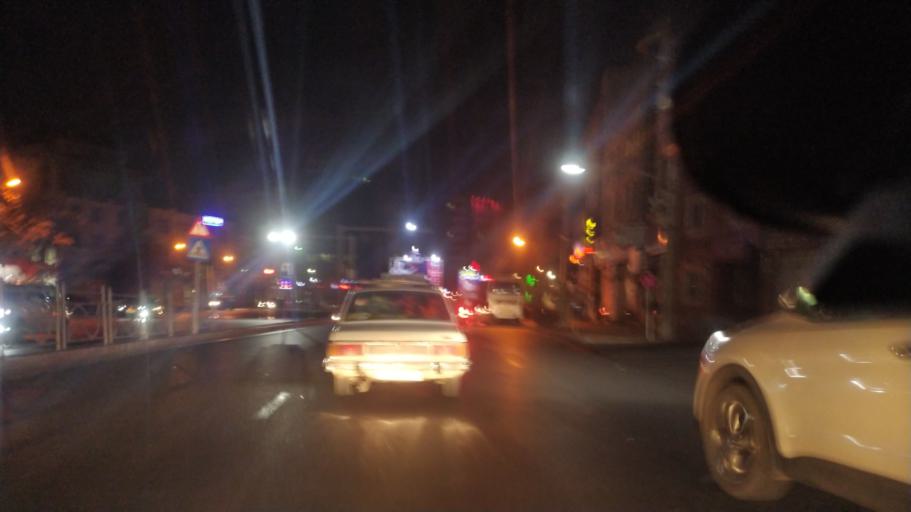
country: IR
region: Alborz
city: Karaj
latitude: 35.8128
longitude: 50.9993
